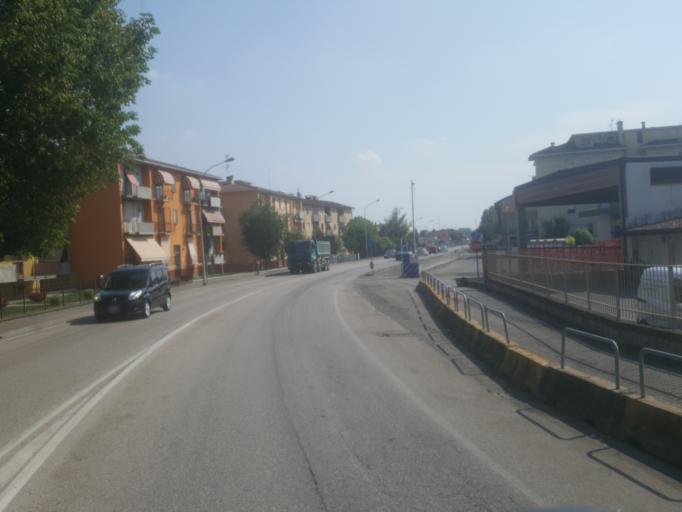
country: IT
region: Lombardy
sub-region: Provincia di Cremona
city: Casalmaggiore
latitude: 44.9885
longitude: 10.4218
